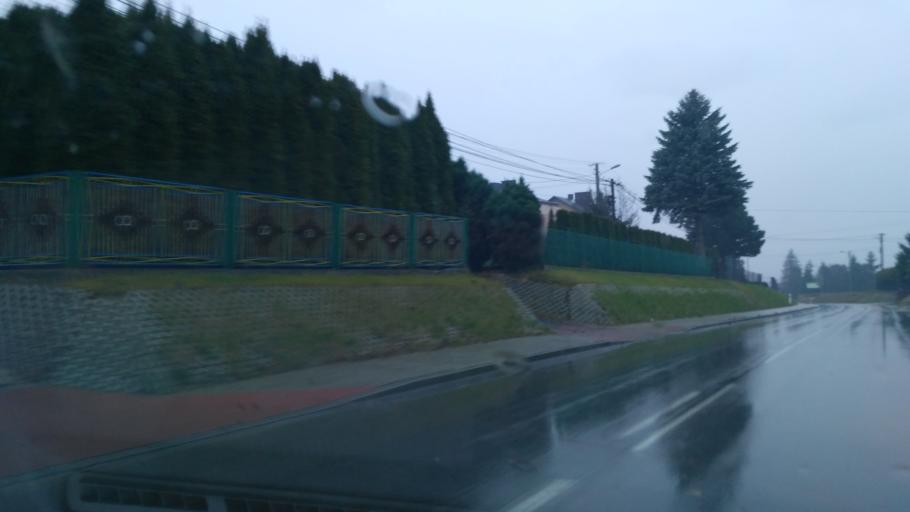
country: PL
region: Subcarpathian Voivodeship
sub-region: Powiat lancucki
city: Krzemienica
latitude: 50.0713
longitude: 22.2024
